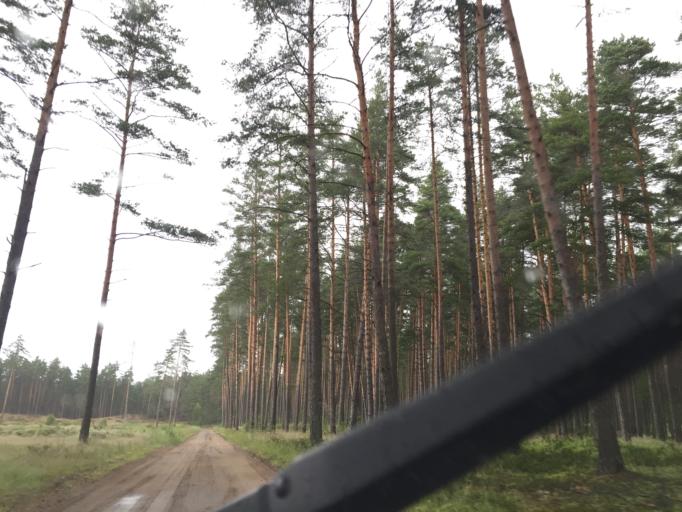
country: LV
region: Riga
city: Jaunciems
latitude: 57.0581
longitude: 24.2014
